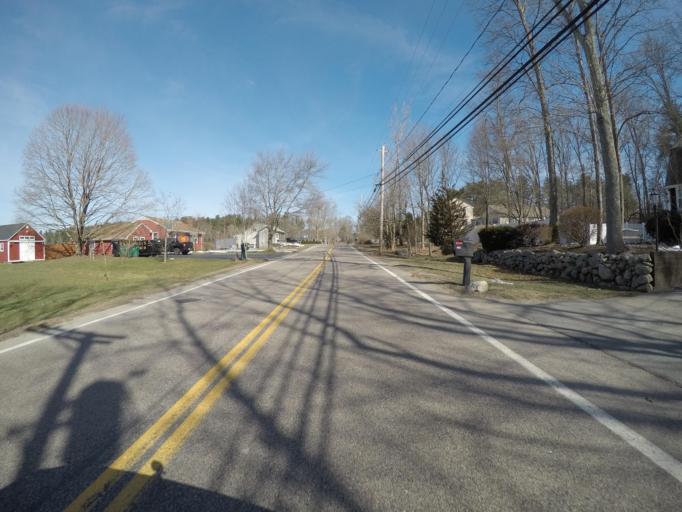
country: US
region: Massachusetts
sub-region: Bristol County
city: Easton
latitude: 42.0151
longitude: -71.1203
